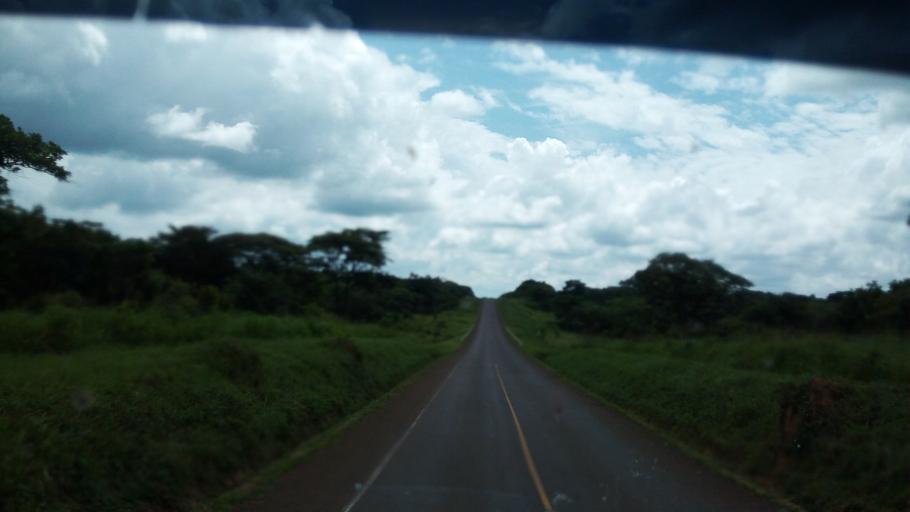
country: UG
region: Northern Region
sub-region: Oyam District
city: Oyam
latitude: 2.3008
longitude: 32.1877
